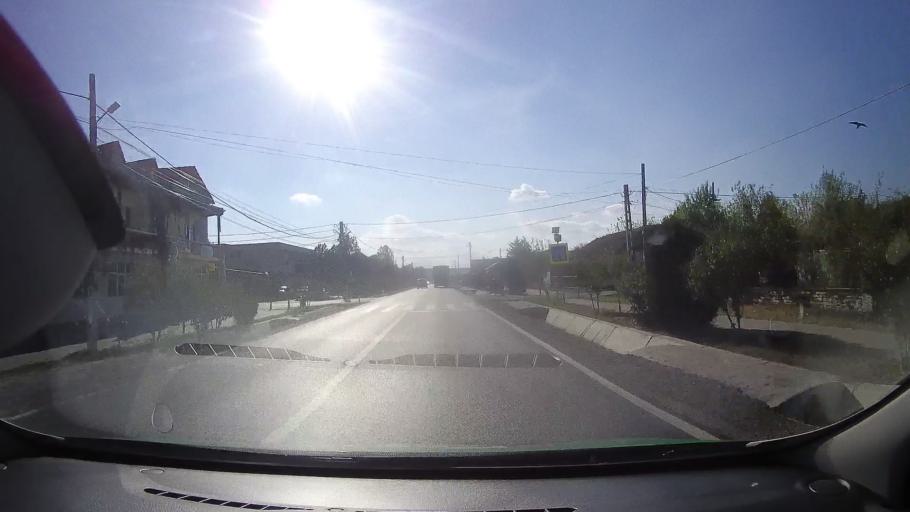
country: RO
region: Tulcea
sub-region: Comuna Baia
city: Baia
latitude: 44.7274
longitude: 28.6807
